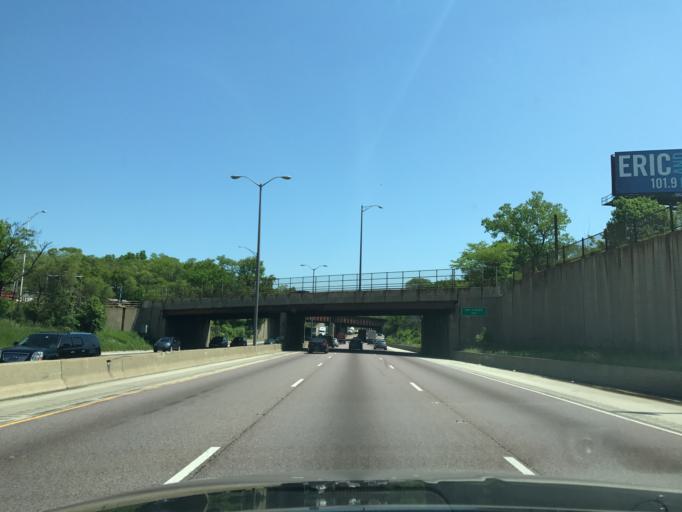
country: US
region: Illinois
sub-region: Cook County
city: Forest Park
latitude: 41.8728
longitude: -87.8166
